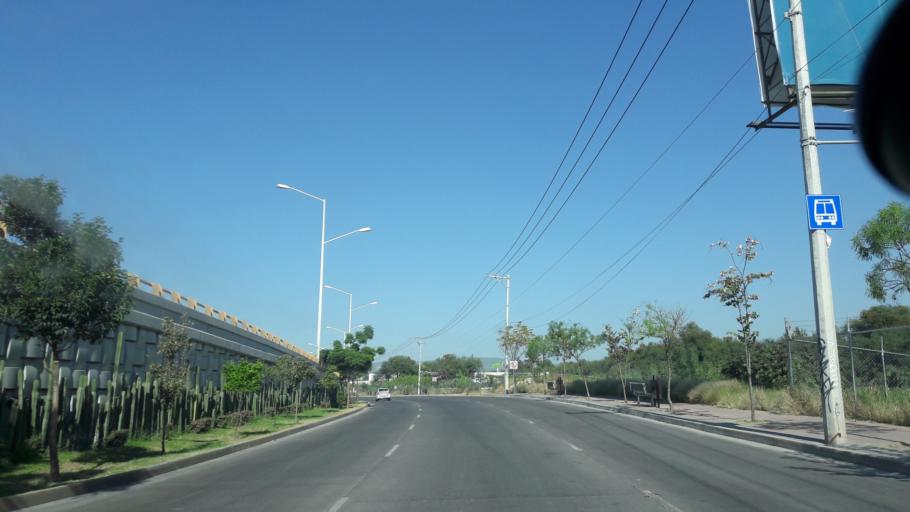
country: MX
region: Guanajuato
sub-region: Leon
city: Medina
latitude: 21.1726
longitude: -101.6586
